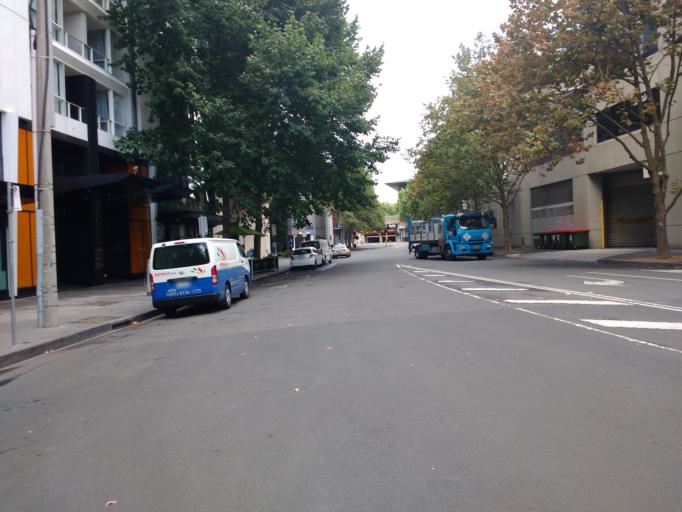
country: AU
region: Victoria
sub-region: Melbourne
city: Southbank
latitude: -37.8228
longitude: 144.9662
